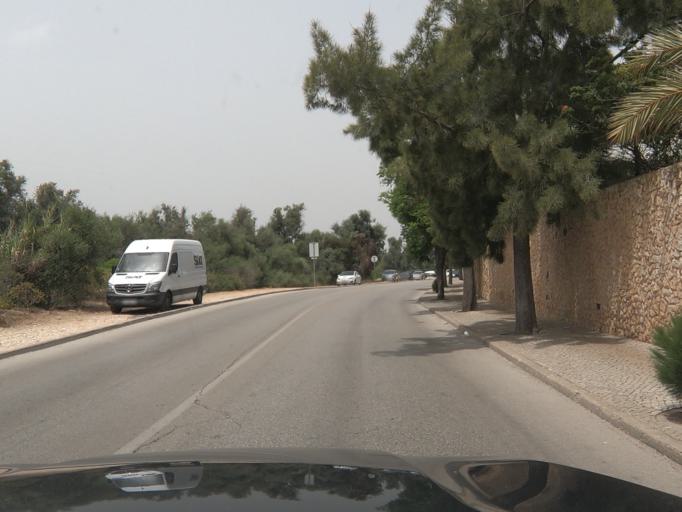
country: PT
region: Faro
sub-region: Portimao
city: Portimao
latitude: 37.1231
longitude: -8.5409
